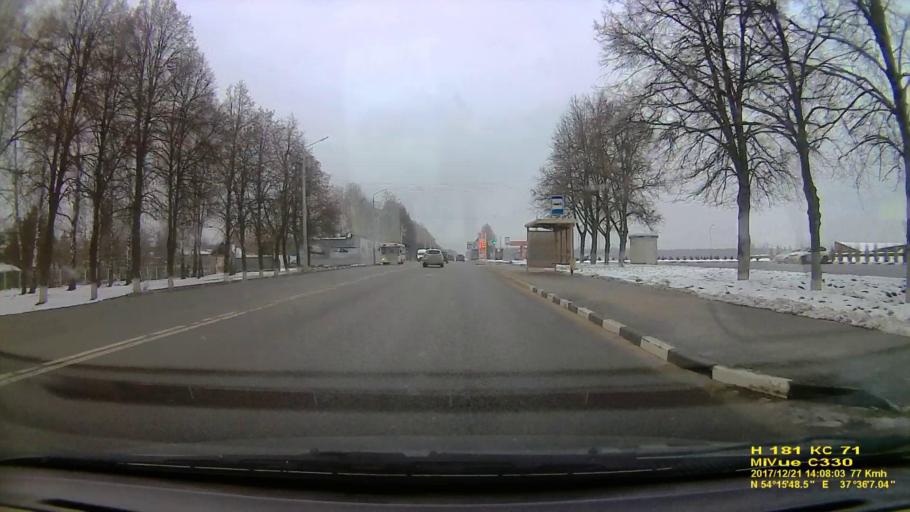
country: RU
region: Tula
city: Gorelki
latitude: 54.2636
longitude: 37.6018
